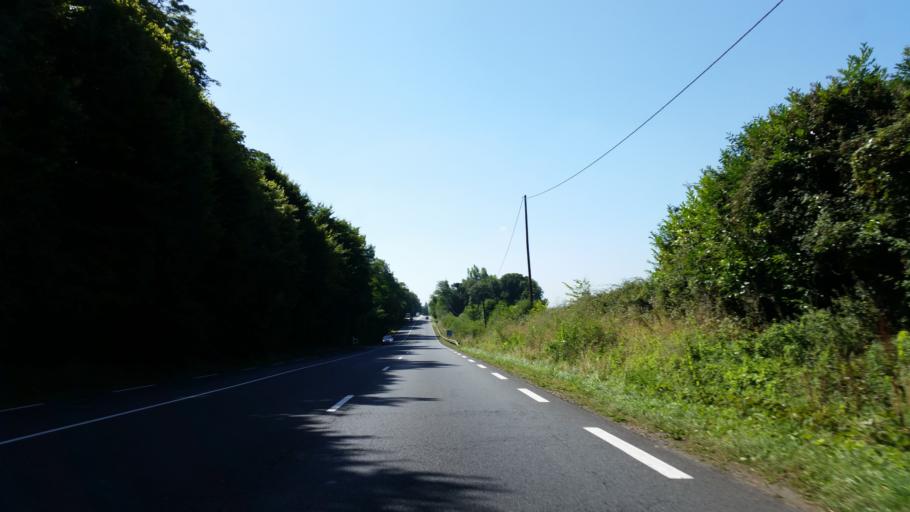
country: FR
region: Lower Normandy
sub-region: Departement du Calvados
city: Lisieux
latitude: 49.2451
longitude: 0.2212
